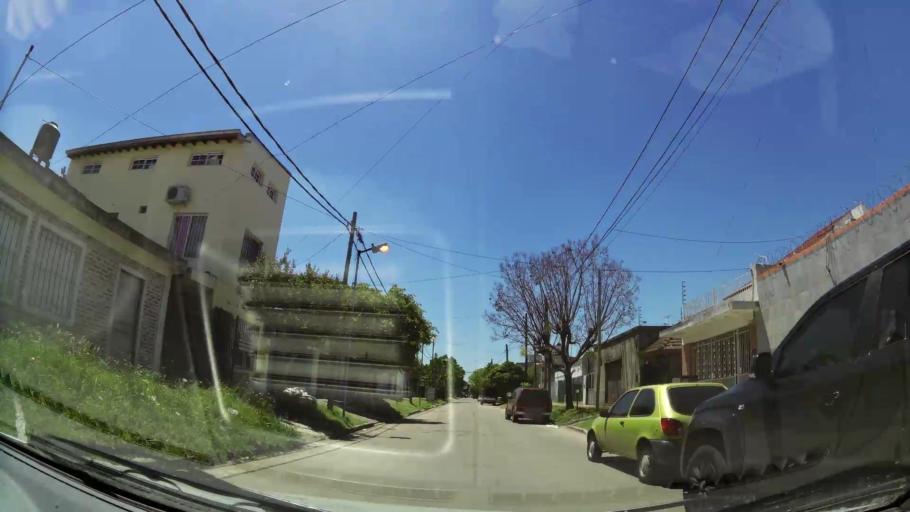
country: AR
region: Buenos Aires
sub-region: Partido de Quilmes
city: Quilmes
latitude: -34.7171
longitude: -58.3114
